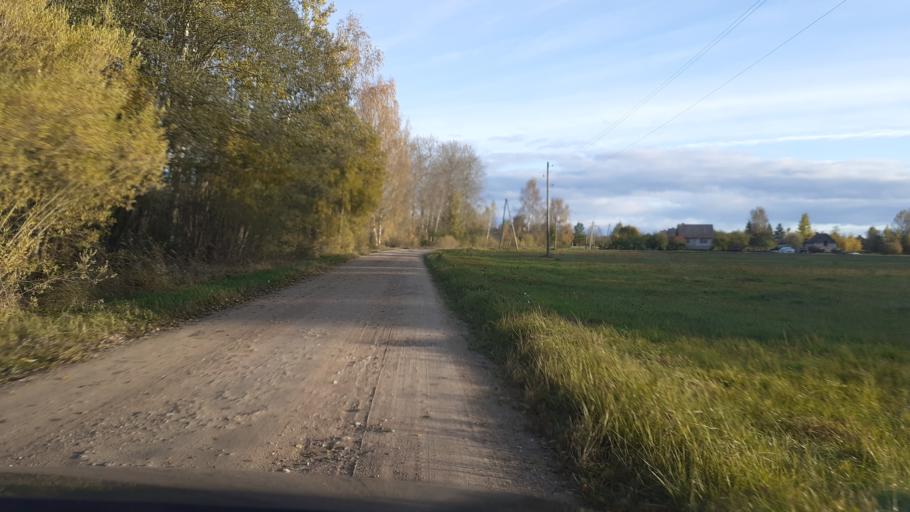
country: LV
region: Kuldigas Rajons
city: Kuldiga
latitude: 56.8785
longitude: 22.1093
